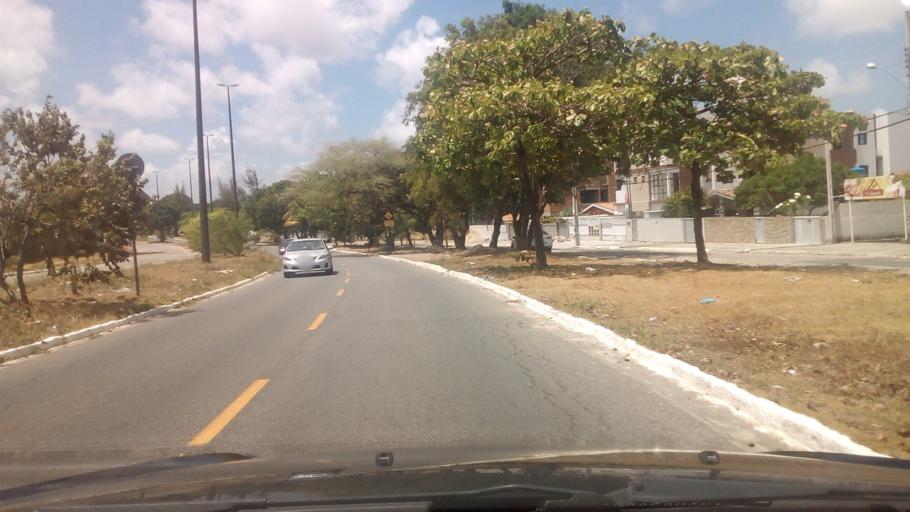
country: BR
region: Paraiba
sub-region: Joao Pessoa
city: Joao Pessoa
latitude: -7.1472
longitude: -34.8348
